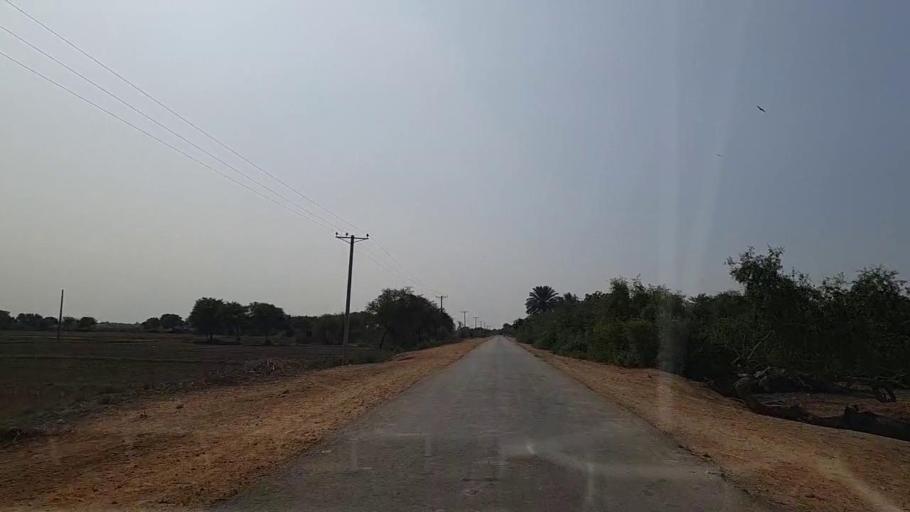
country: PK
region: Sindh
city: Chuhar Jamali
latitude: 24.3525
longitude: 67.9546
